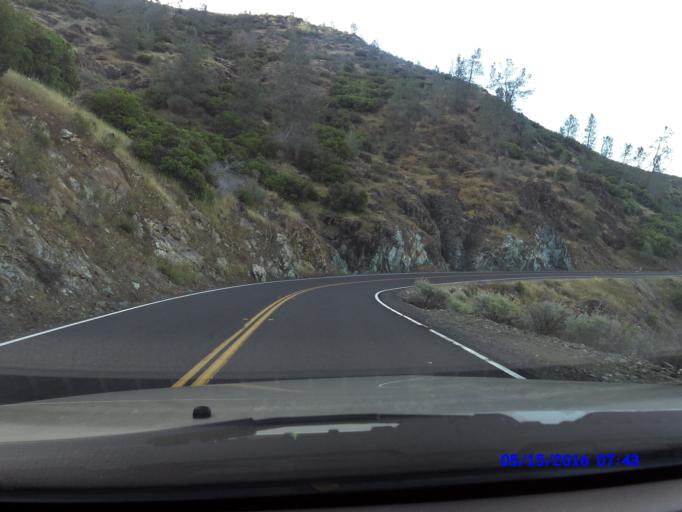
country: US
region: California
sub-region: Mariposa County
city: Mariposa
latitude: 37.6441
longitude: -120.1465
